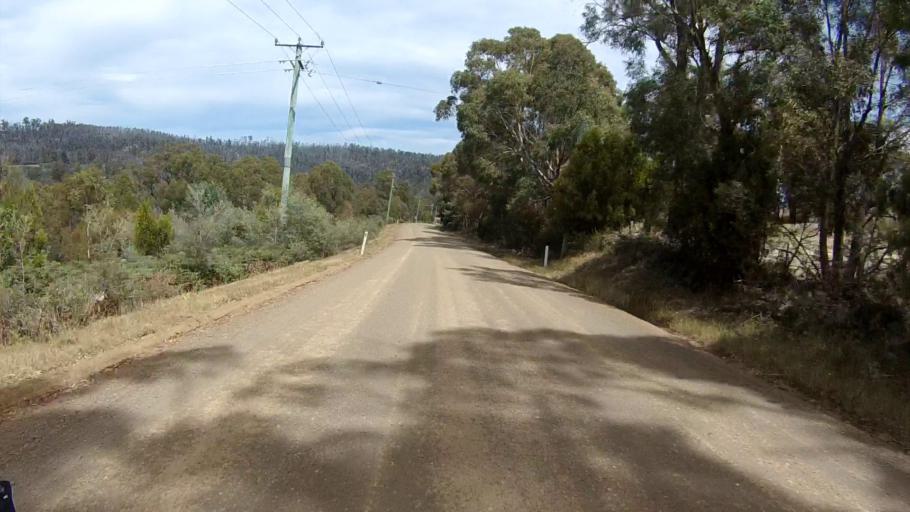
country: AU
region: Tasmania
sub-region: Sorell
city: Sorell
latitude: -42.8019
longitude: 147.6759
